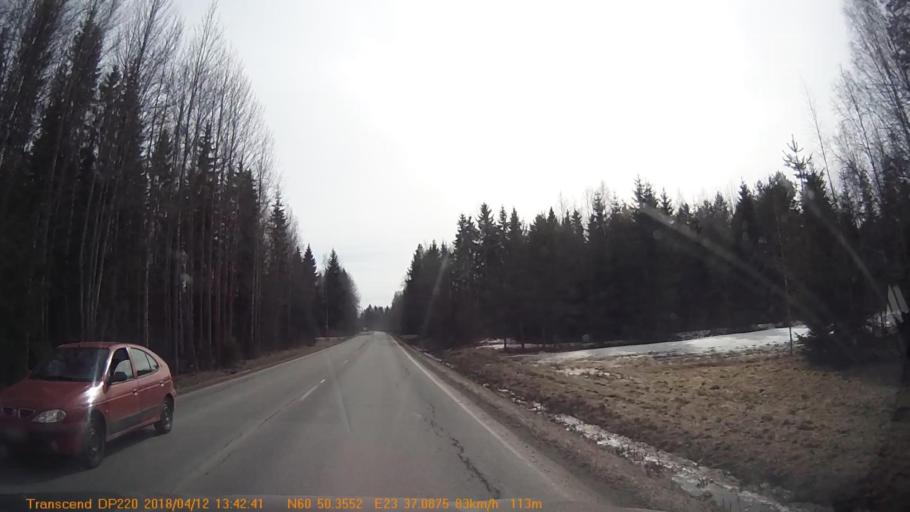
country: FI
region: Haeme
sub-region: Forssa
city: Forssa
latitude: 60.8385
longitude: 23.6181
